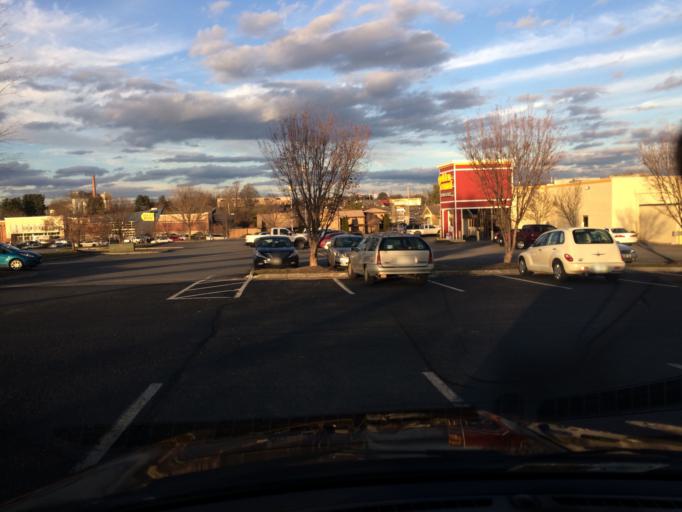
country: US
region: Virginia
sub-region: Montgomery County
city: Merrimac
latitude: 37.1648
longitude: -80.4247
